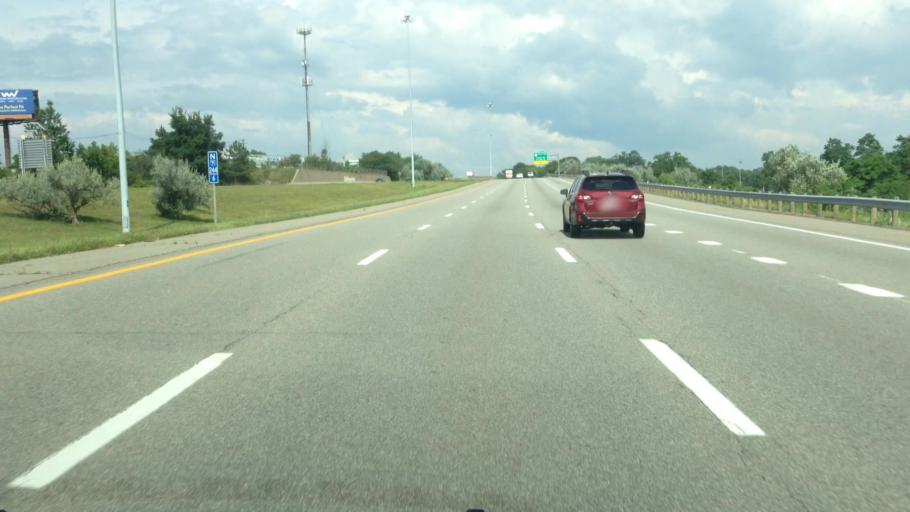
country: US
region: Ohio
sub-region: Cuyahoga County
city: Brooklyn
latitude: 41.4515
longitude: -81.7287
